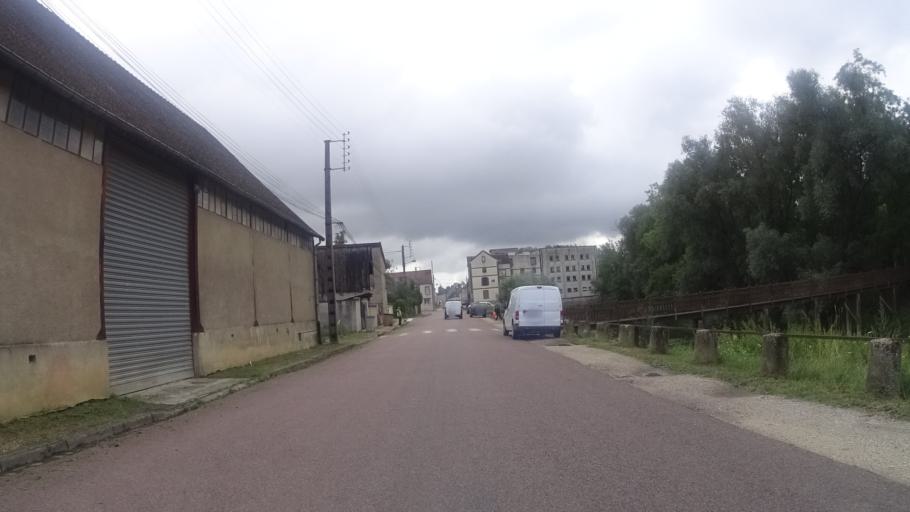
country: FR
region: Bourgogne
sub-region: Departement de l'Yonne
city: Brienon-sur-Armancon
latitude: 47.9856
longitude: 3.6142
